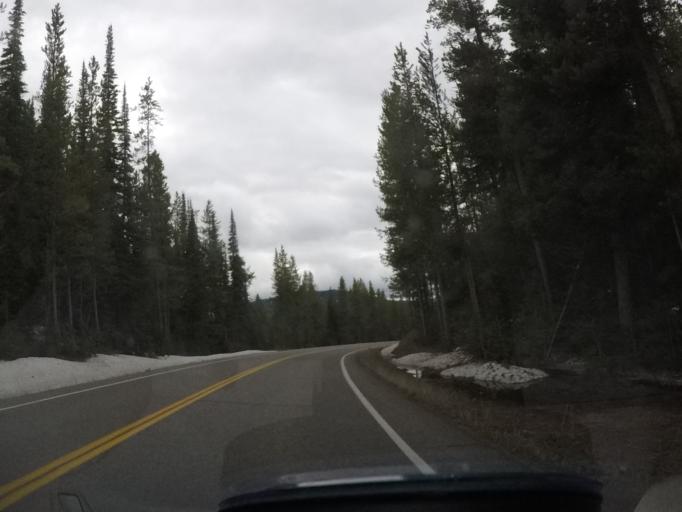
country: US
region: Wyoming
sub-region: Teton County
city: Moose Wilson Road
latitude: 43.9569
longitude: -110.6366
